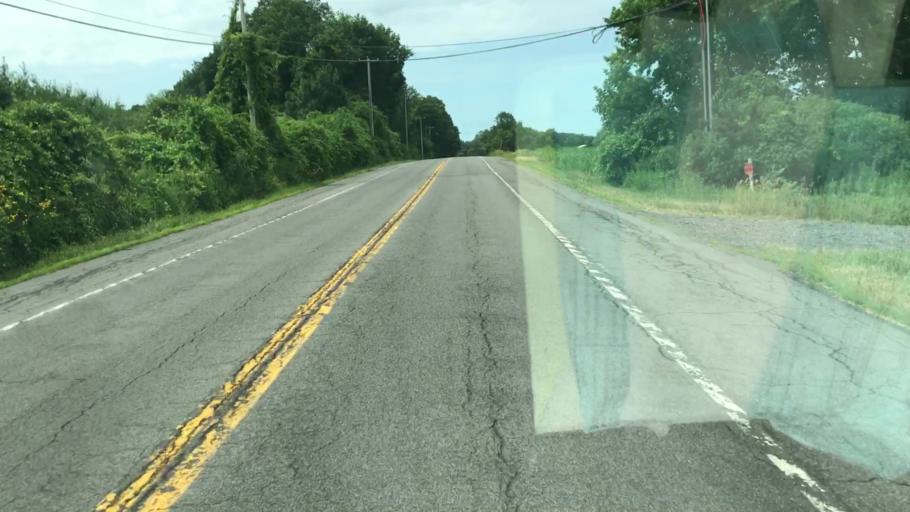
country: US
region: New York
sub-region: Onondaga County
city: Nedrow
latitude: 42.9111
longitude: -76.2236
